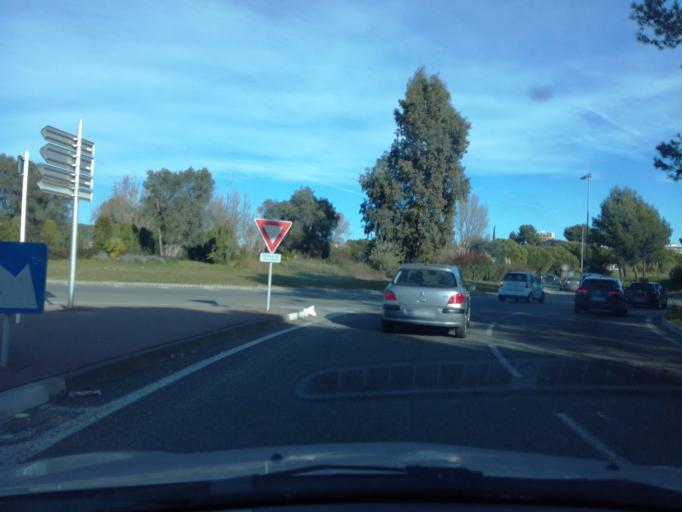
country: FR
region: Provence-Alpes-Cote d'Azur
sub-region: Departement des Alpes-Maritimes
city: Vallauris
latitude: 43.5780
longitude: 7.0906
